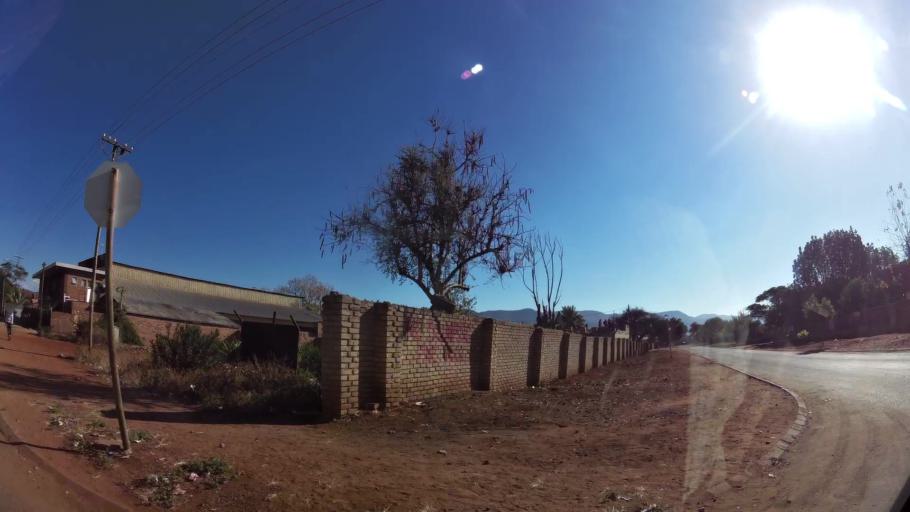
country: ZA
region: Limpopo
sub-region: Waterberg District Municipality
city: Mokopane
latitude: -24.1782
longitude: 28.9944
